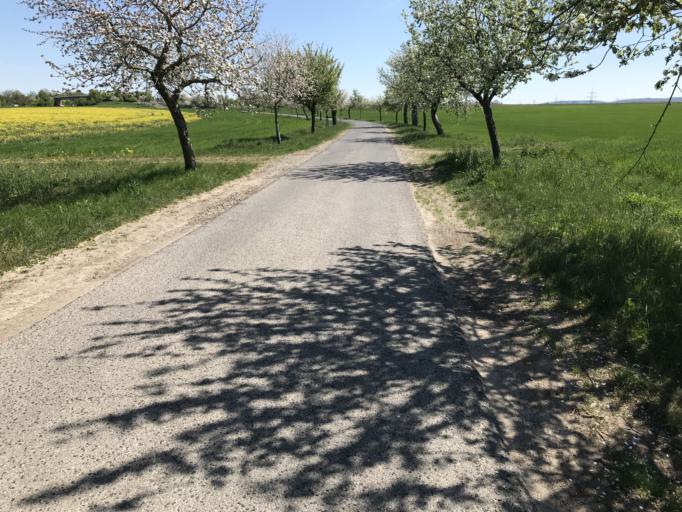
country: DE
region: Bavaria
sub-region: Regierungsbezirk Unterfranken
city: Markt Einersheim
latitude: 49.6872
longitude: 10.2740
